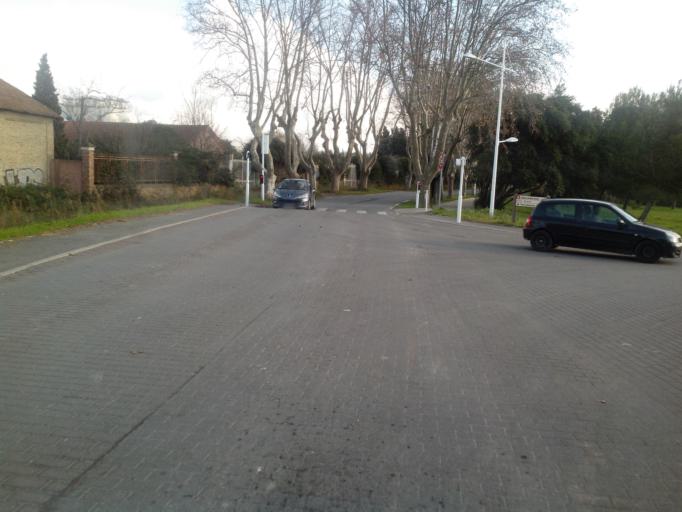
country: FR
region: Provence-Alpes-Cote d'Azur
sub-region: Departement des Bouches-du-Rhone
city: Port-Saint-Louis-du-Rhone
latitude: 43.4198
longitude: 4.7336
